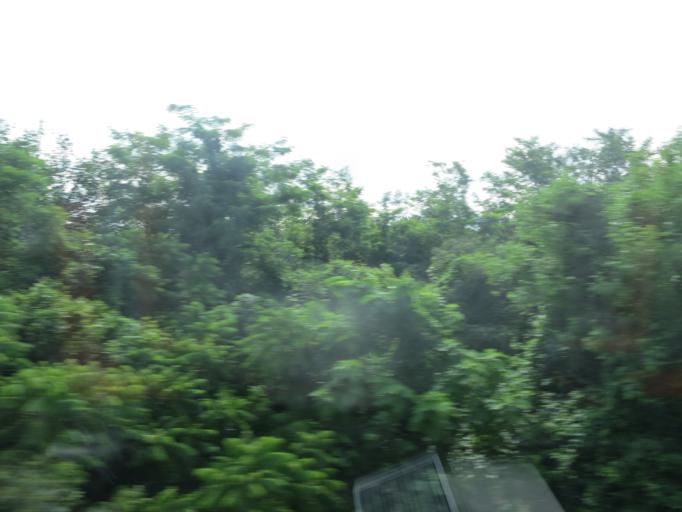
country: GE
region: Imereti
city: Samtredia
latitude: 42.1146
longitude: 42.3272
